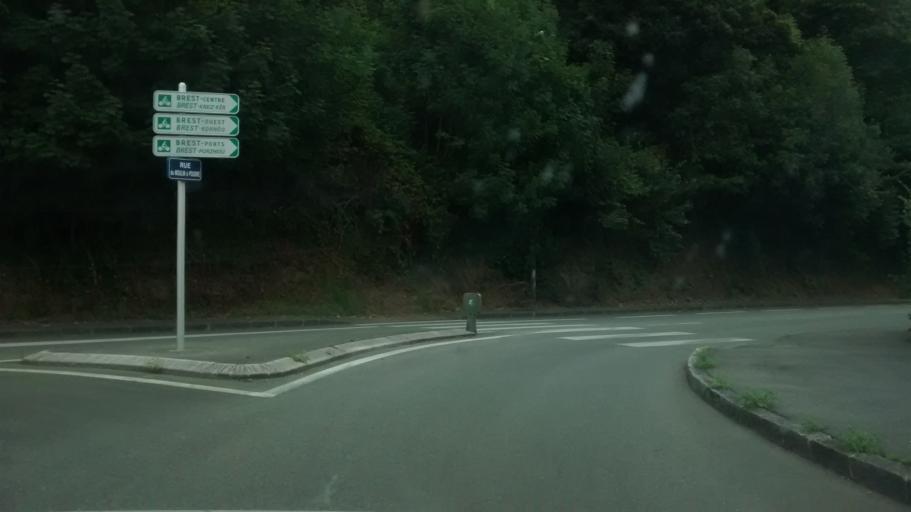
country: FR
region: Brittany
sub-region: Departement du Finistere
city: Brest
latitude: 48.3991
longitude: -4.4914
